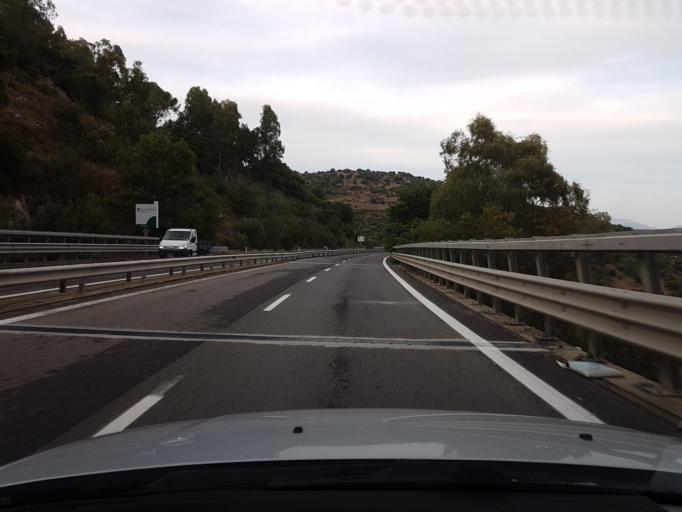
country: IT
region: Sardinia
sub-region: Provincia di Nuoro
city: Nuoro
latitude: 40.3374
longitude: 9.3010
